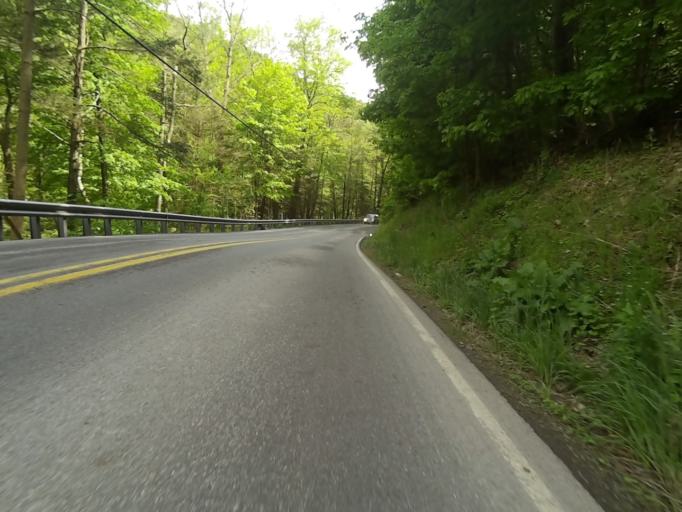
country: US
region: Pennsylvania
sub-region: Centre County
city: Zion
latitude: 41.0053
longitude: -77.6432
